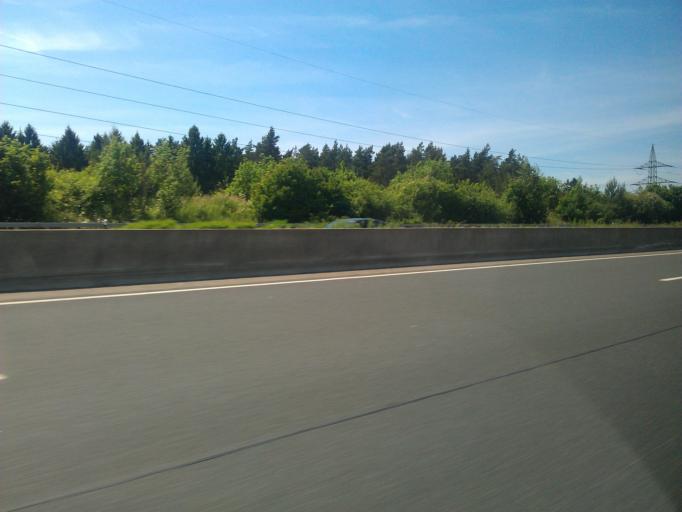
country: DE
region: Rheinland-Pfalz
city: Windhagen
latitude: 50.6466
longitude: 7.3351
